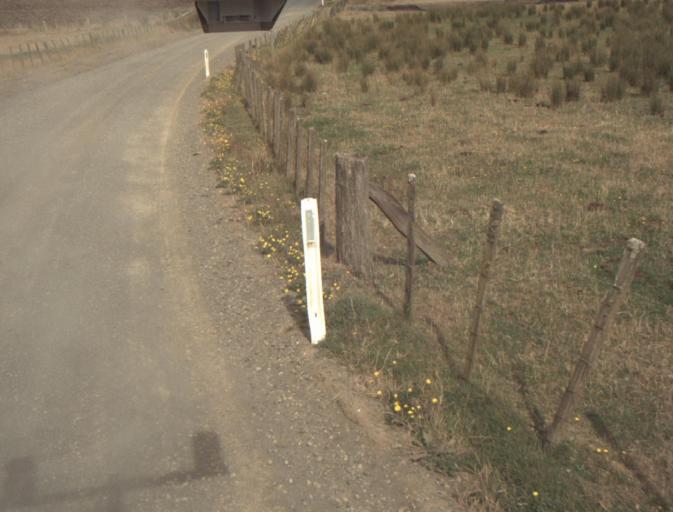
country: AU
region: Tasmania
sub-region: Dorset
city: Scottsdale
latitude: -41.4733
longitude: 147.5832
